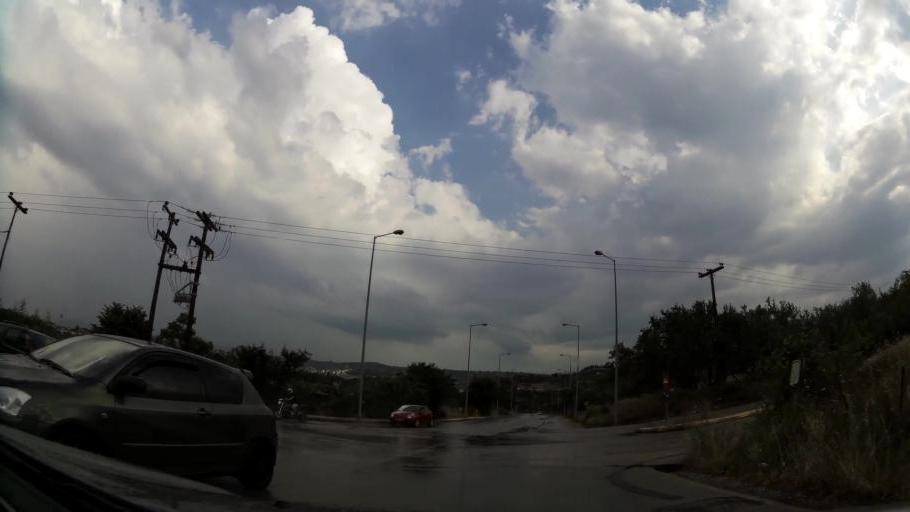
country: GR
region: Central Macedonia
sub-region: Nomos Imathias
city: Veroia
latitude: 40.5366
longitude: 22.1971
